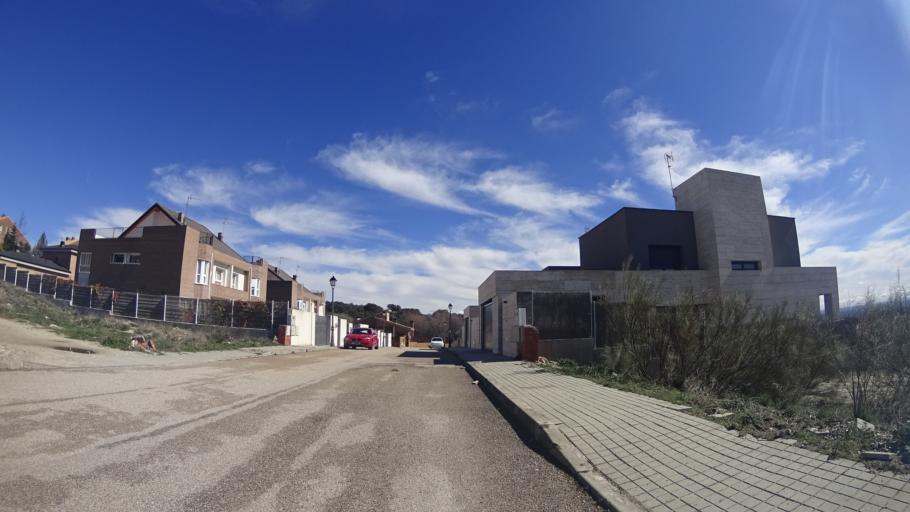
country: ES
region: Madrid
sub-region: Provincia de Madrid
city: Torrelodones
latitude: 40.5783
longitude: -3.9184
